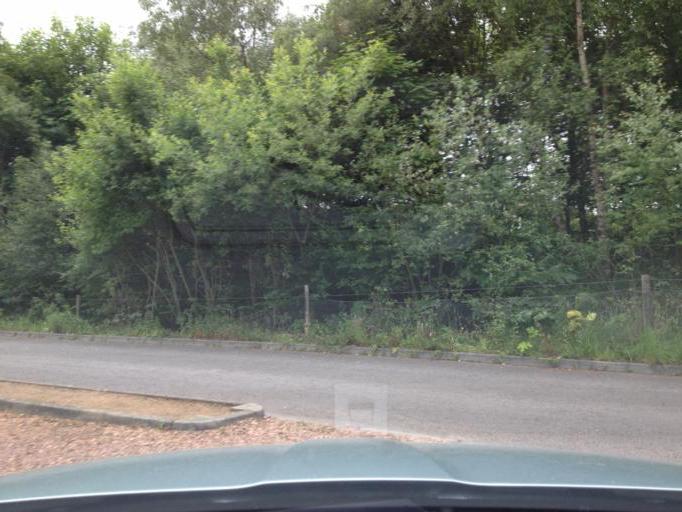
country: GB
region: Scotland
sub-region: Fife
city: Strathkinness
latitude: 56.3166
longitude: -2.8437
